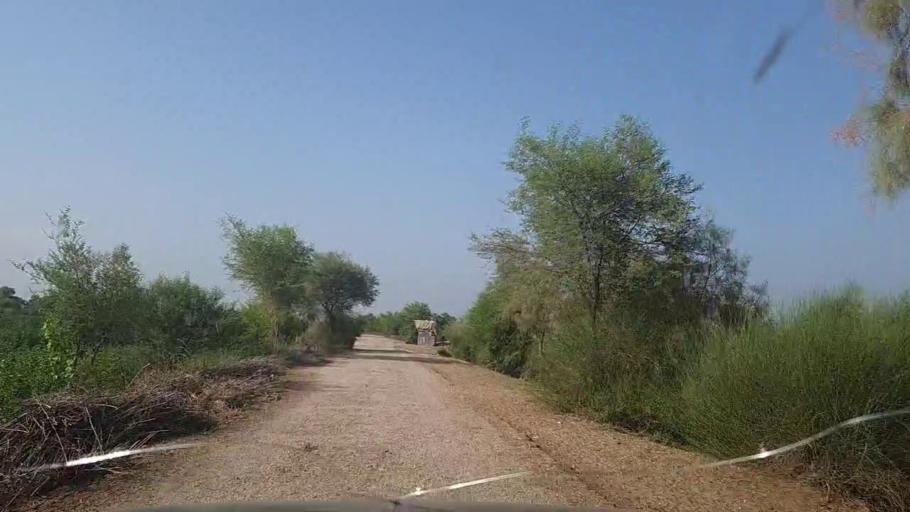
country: PK
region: Sindh
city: Khanpur
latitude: 27.7114
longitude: 69.3319
